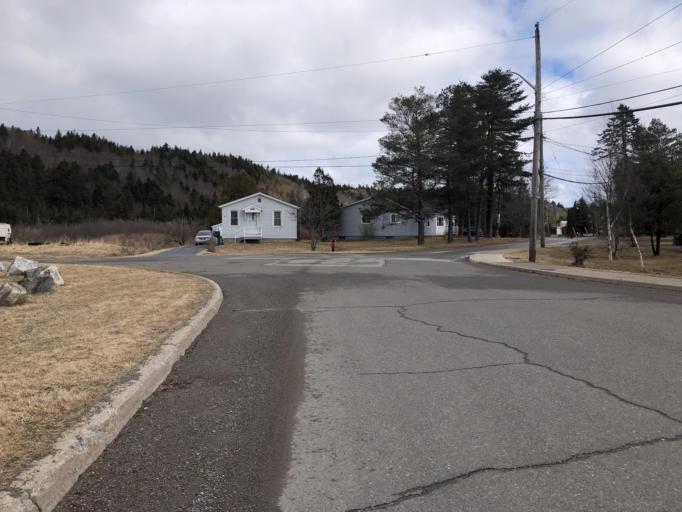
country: CA
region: New Brunswick
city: Saint John
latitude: 45.3230
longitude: -66.0134
